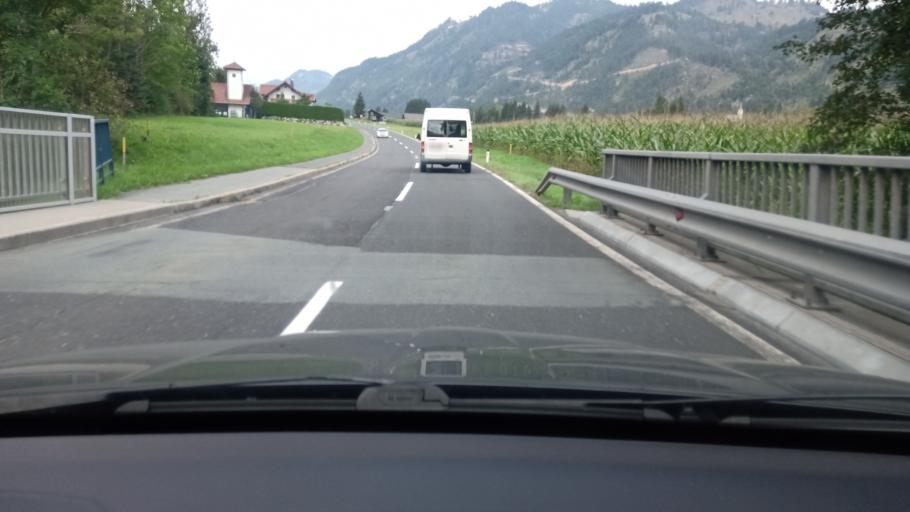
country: AT
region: Carinthia
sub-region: Politischer Bezirk Hermagor
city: Hermagor
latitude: 46.6607
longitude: 13.3122
